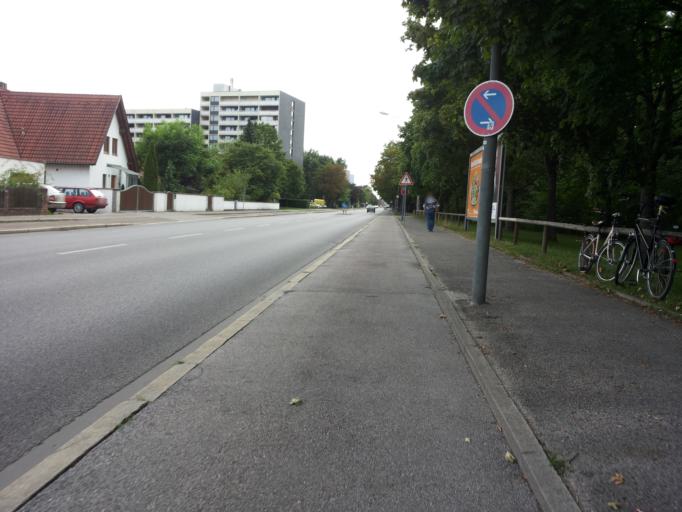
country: DE
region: Bavaria
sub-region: Upper Bavaria
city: Ingolstadt
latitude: 48.7829
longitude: 11.4113
